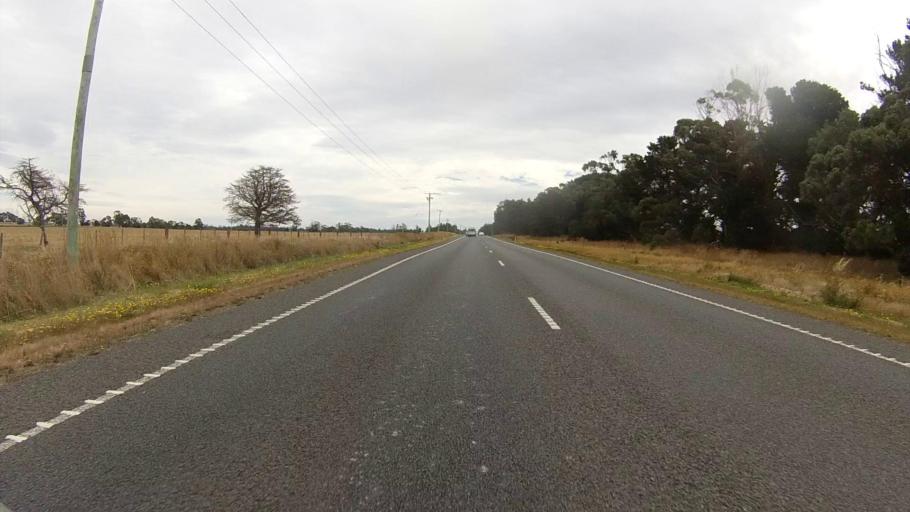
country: AU
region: Tasmania
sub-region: Northern Midlands
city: Evandale
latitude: -41.6951
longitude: 147.2864
